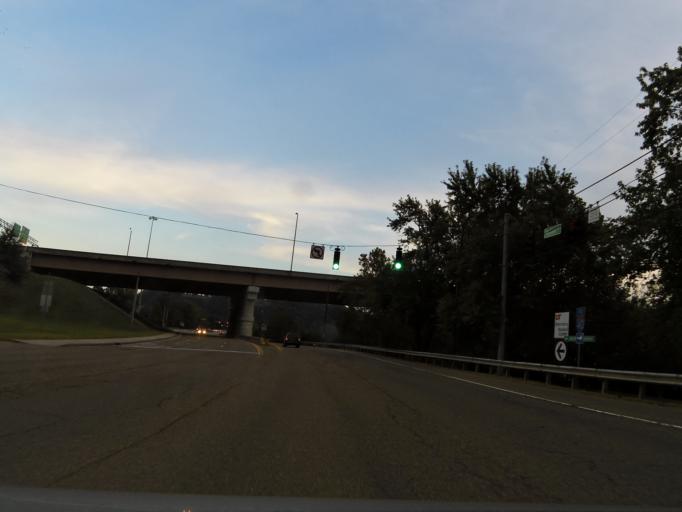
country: US
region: Tennessee
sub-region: Knox County
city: Knoxville
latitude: 35.9488
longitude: -83.9459
